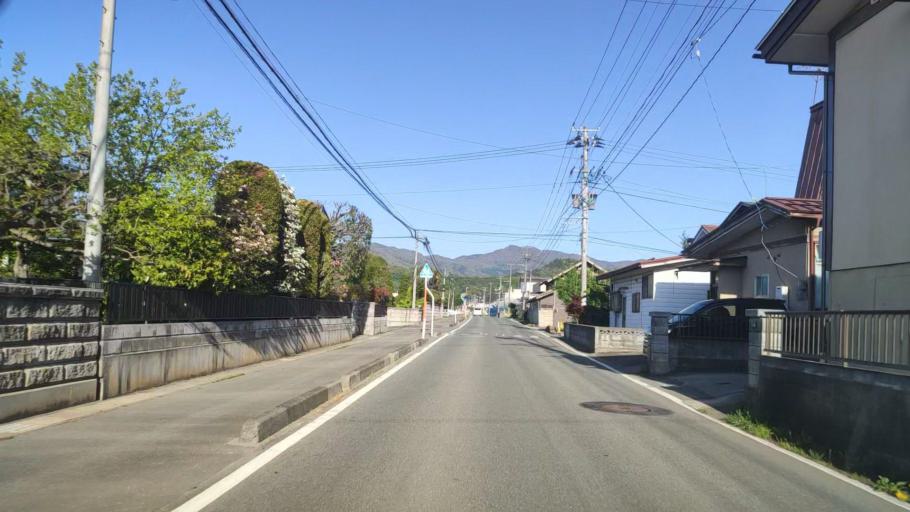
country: JP
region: Yamagata
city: Tendo
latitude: 38.3559
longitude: 140.3568
